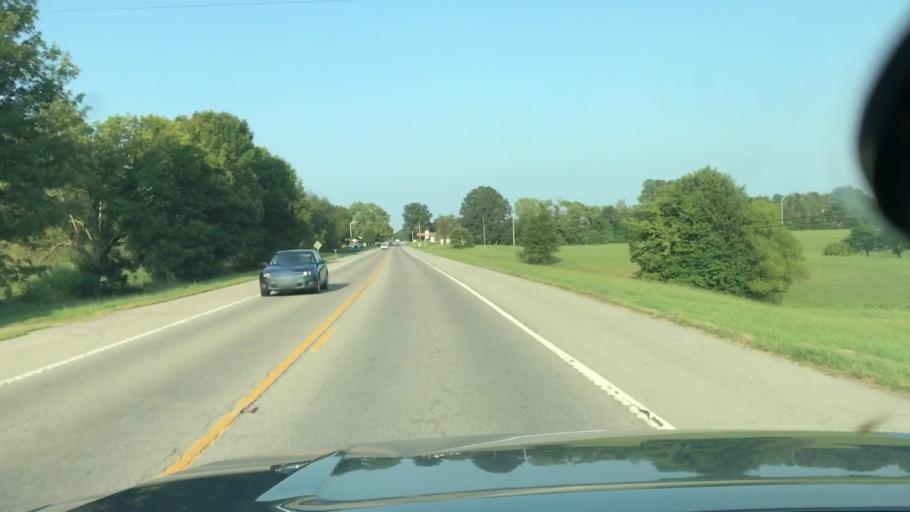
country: US
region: Tennessee
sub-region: Sumner County
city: Portland
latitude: 36.5776
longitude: -86.4428
